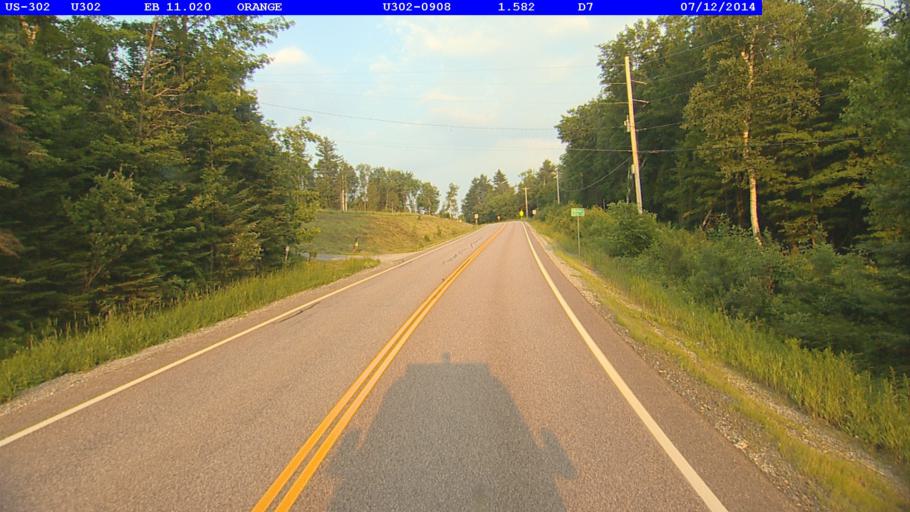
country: US
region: Vermont
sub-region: Washington County
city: South Barre
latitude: 44.1498
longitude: -72.4075
